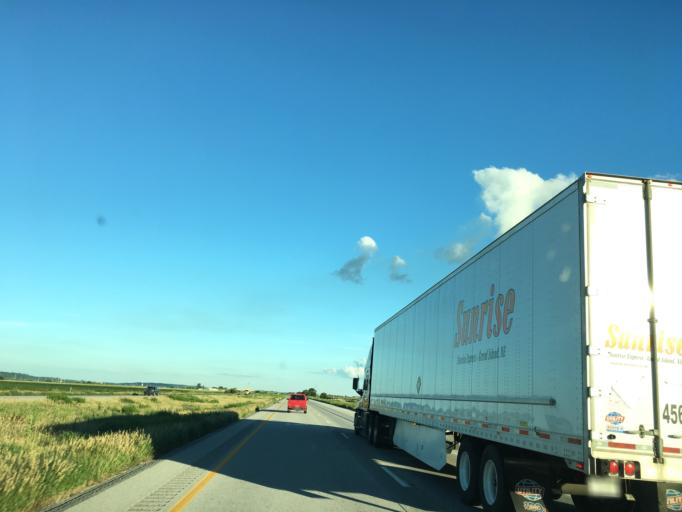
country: US
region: Iowa
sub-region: Fremont County
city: Hamburg
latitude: 40.6520
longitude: -95.7498
